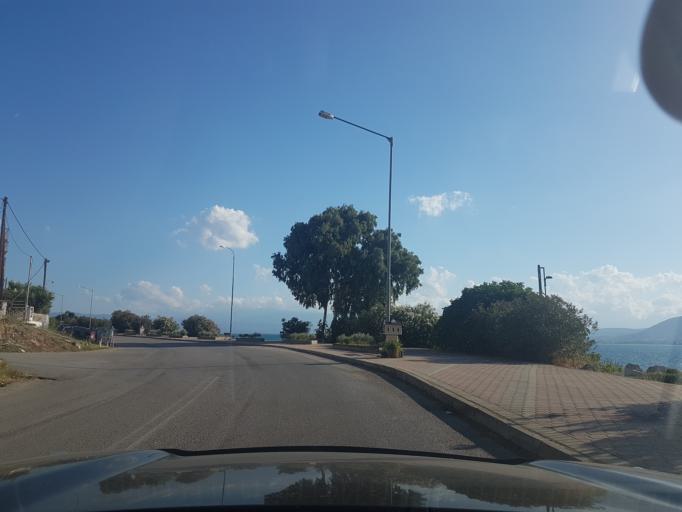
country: GR
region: Central Greece
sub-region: Nomos Evvoias
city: Chalkida
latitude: 38.4727
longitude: 23.5915
